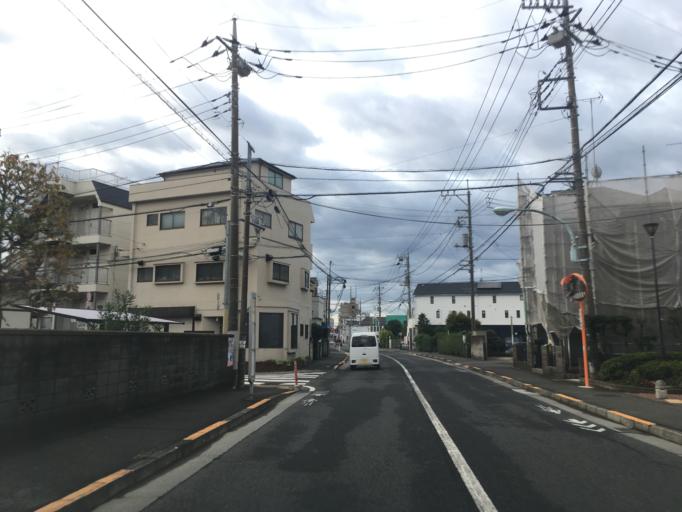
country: JP
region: Tokyo
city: Kokubunji
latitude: 35.7202
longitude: 139.4648
